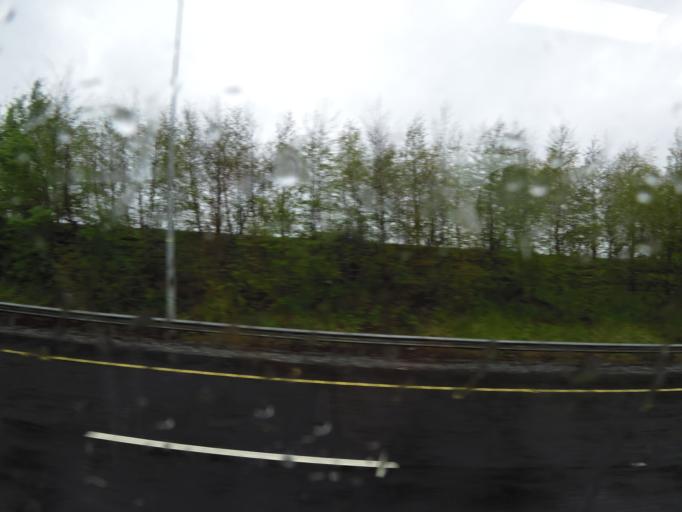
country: IE
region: Leinster
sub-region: Kildare
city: Celbridge
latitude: 53.3590
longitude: -6.5258
